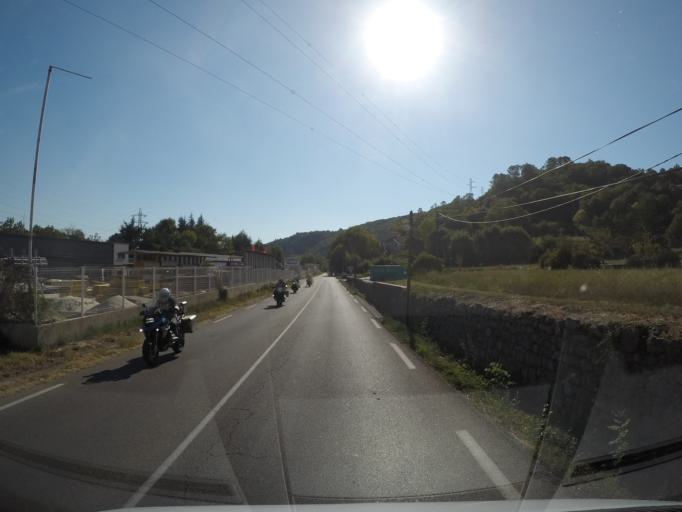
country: FR
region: Languedoc-Roussillon
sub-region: Departement du Gard
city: Anduze
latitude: 44.0409
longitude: 3.9854
